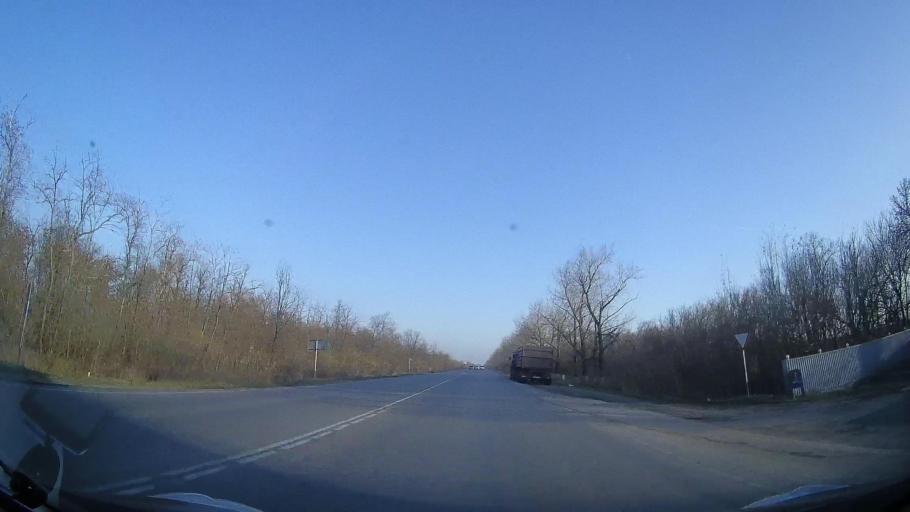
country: RU
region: Rostov
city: Bataysk
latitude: 47.0644
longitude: 39.8087
